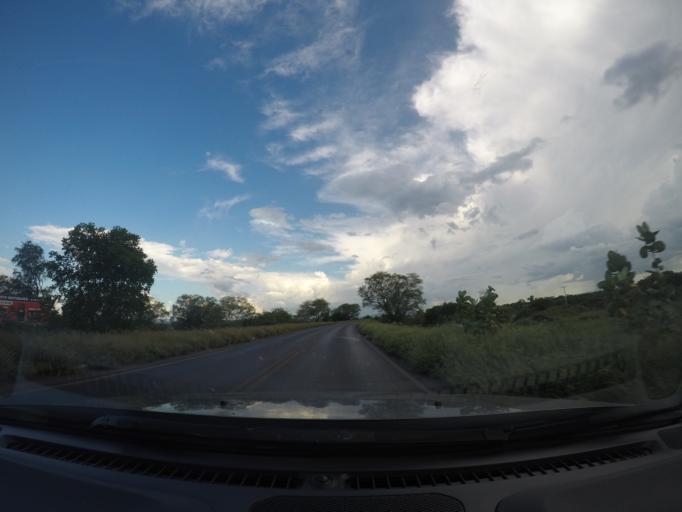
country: BR
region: Bahia
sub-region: Ibotirama
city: Ibotirama
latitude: -12.1433
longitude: -43.3169
